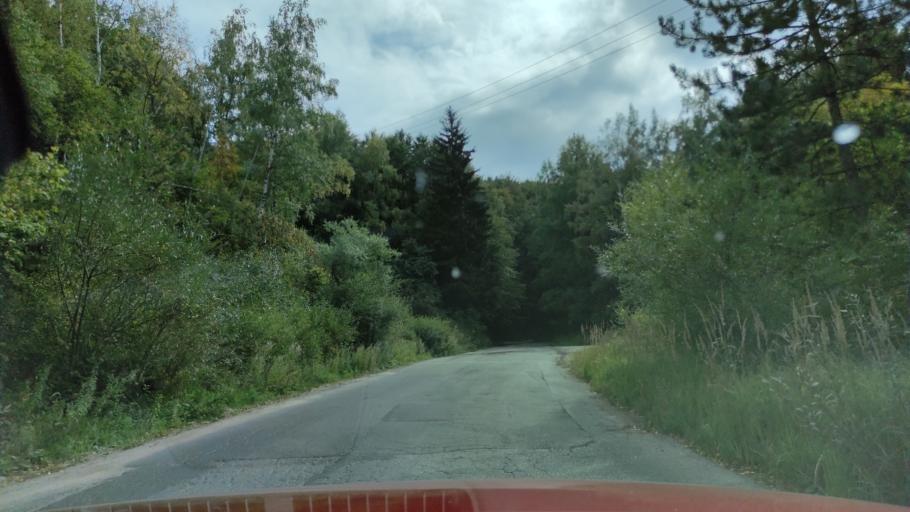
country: BG
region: Sofia-Capital
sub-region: Stolichna Obshtina
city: Sofia
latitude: 42.6196
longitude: 23.2261
